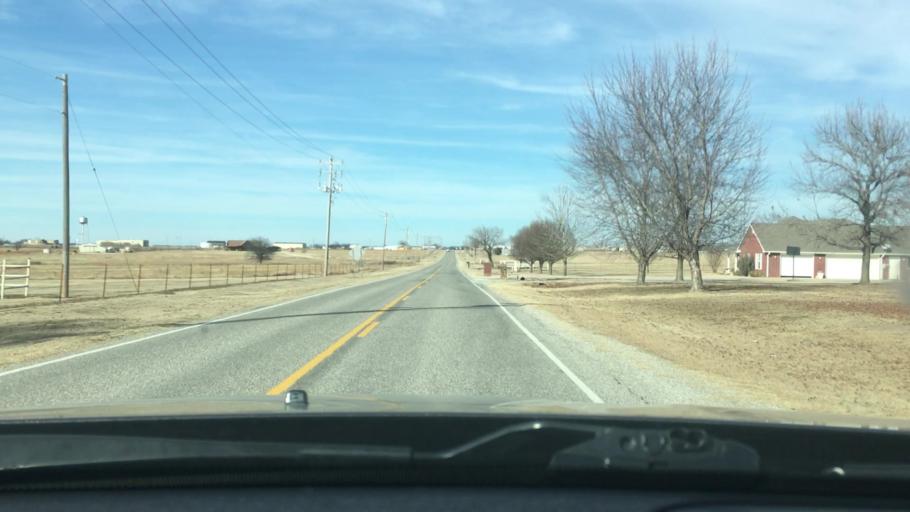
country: US
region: Oklahoma
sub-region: Murray County
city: Davis
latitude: 34.4978
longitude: -97.0904
